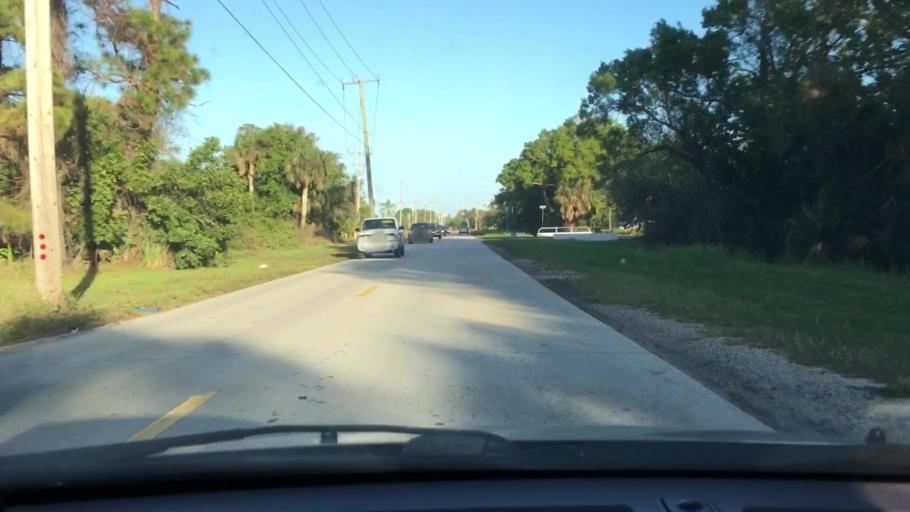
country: US
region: Florida
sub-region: Indian River County
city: Vero Beach South
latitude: 27.6460
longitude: -80.4338
